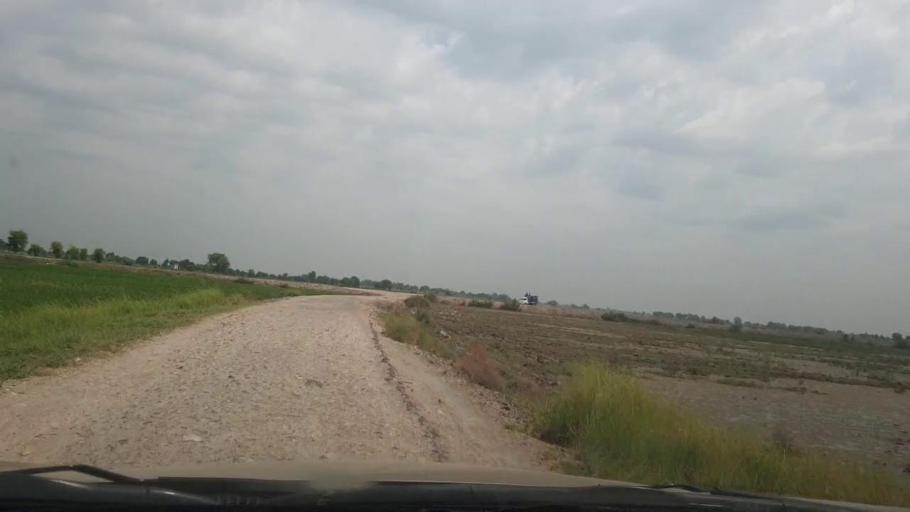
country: PK
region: Sindh
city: Ratodero
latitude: 27.7221
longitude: 68.2324
